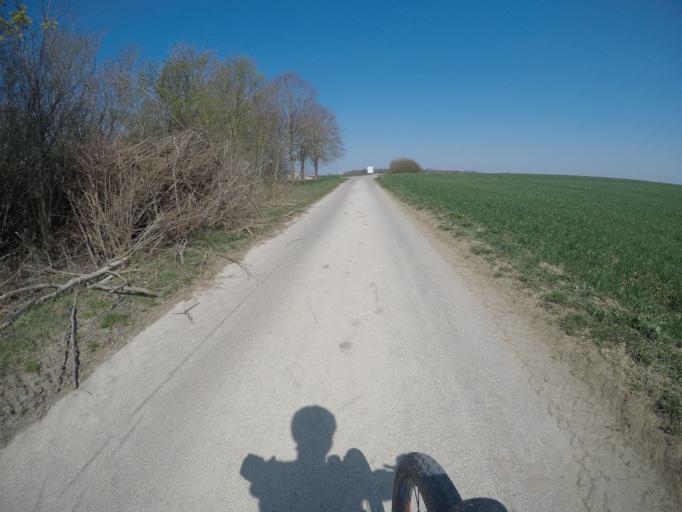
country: DE
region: Baden-Wuerttemberg
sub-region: Regierungsbezirk Stuttgart
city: Renningen
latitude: 48.7390
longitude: 8.9225
